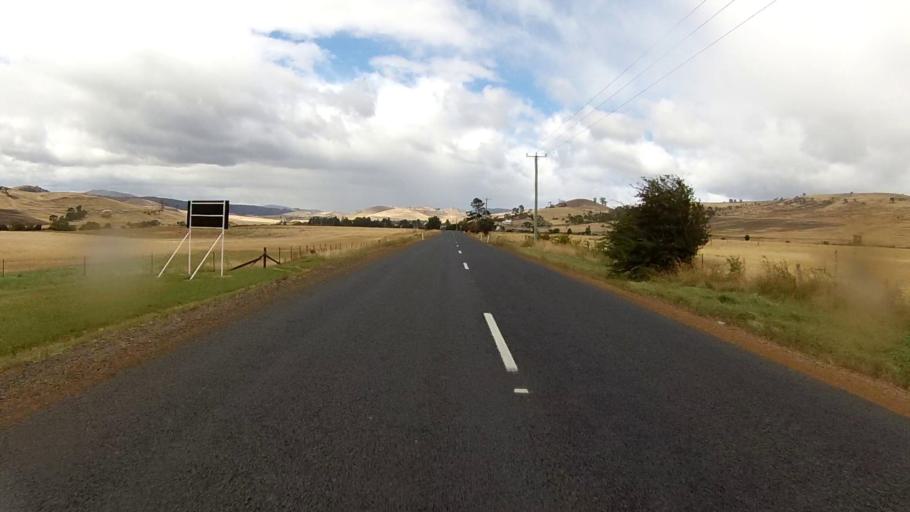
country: AU
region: Tasmania
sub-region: Brighton
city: Bridgewater
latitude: -42.5262
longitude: 147.3586
